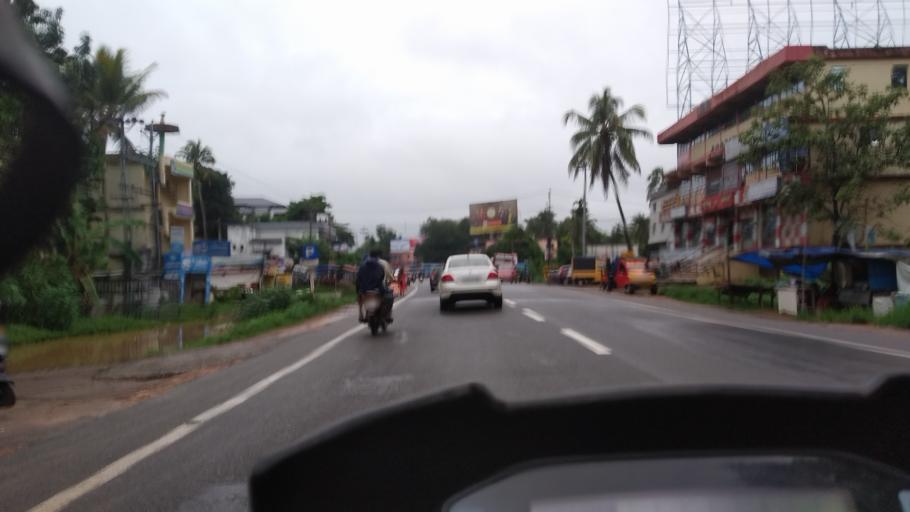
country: IN
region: Kerala
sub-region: Alappuzha
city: Mavelikara
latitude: 9.2773
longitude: 76.4598
